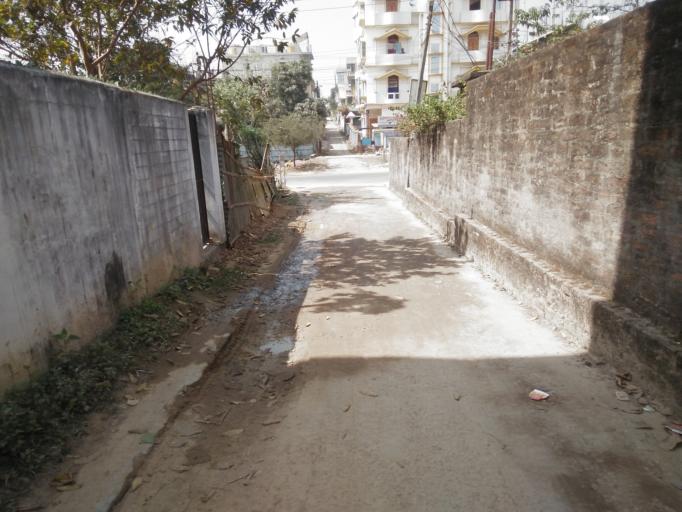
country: IN
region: Tripura
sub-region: West Tripura
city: Agartala
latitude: 23.8699
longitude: 91.2978
